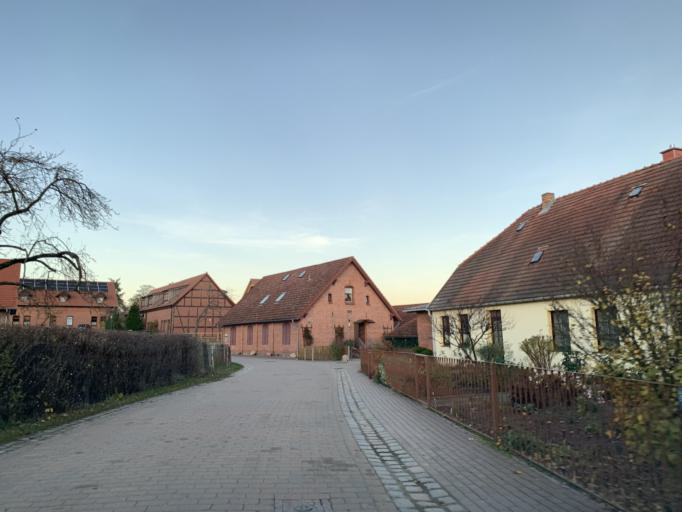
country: DE
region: Mecklenburg-Vorpommern
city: Loitz
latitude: 53.3386
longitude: 13.4437
